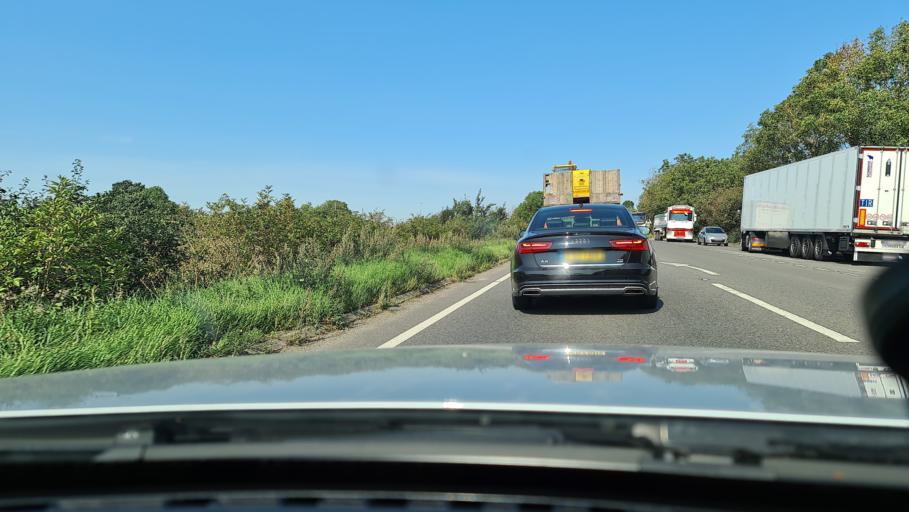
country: GB
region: England
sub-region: Leicestershire
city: Lutterworth
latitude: 52.4203
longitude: -1.2232
